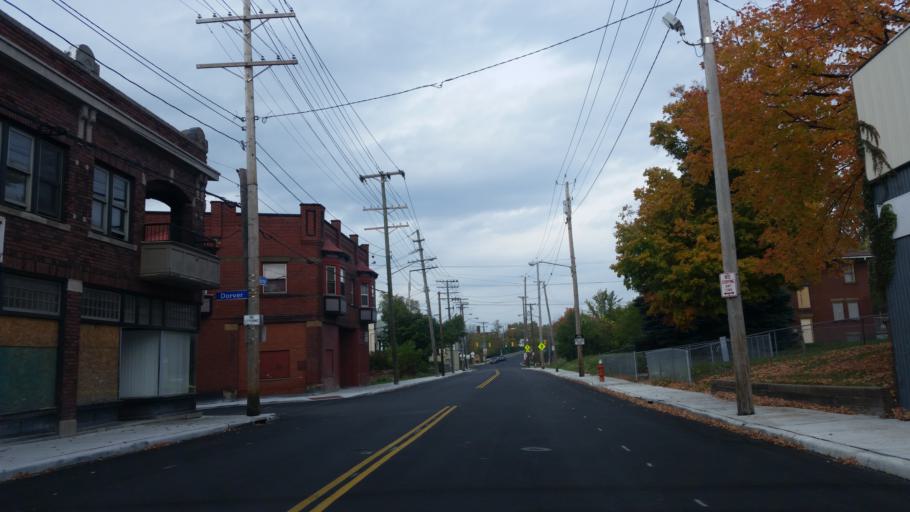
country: US
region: Ohio
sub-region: Cuyahoga County
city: Garfield Heights
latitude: 41.4425
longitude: -81.6258
